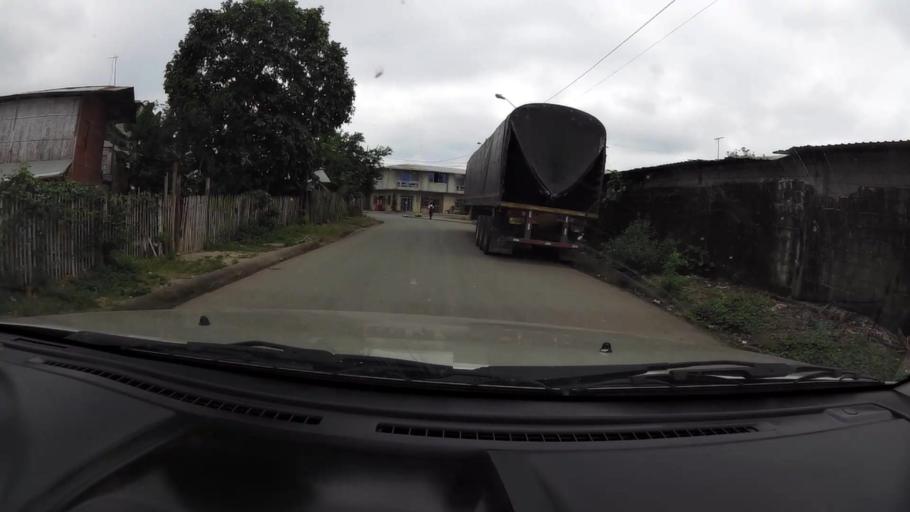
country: EC
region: El Oro
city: Pasaje
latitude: -3.2359
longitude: -79.8266
